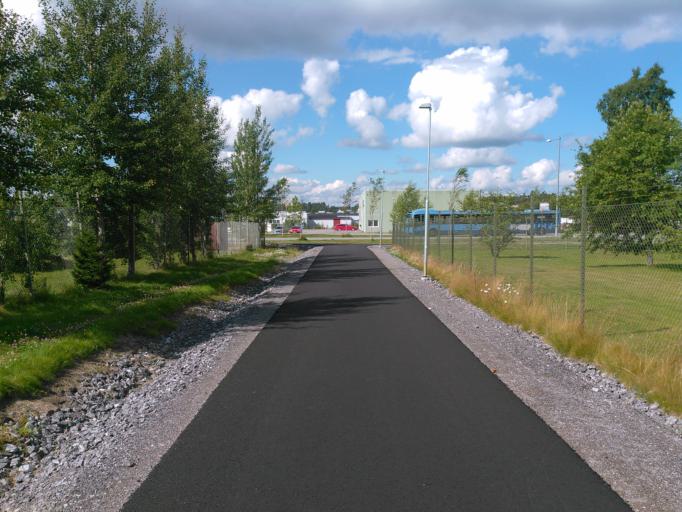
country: SE
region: Vaesterbotten
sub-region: Umea Kommun
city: Ersmark
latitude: 63.8501
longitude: 20.3165
